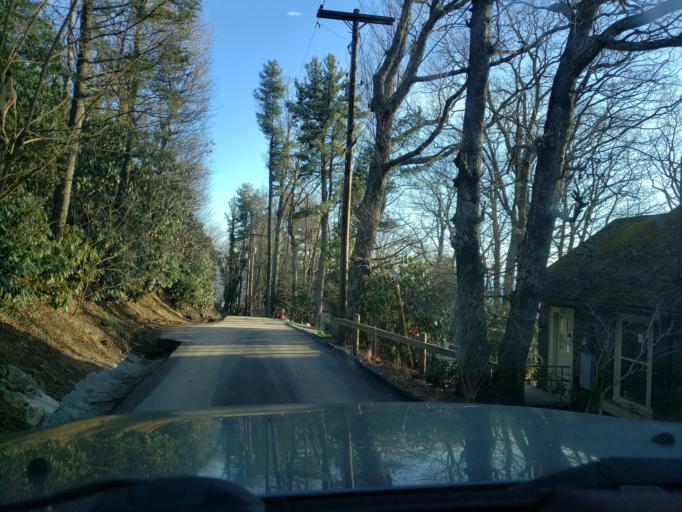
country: US
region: North Carolina
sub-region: Watauga County
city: Blowing Rock
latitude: 36.1231
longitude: -81.6775
